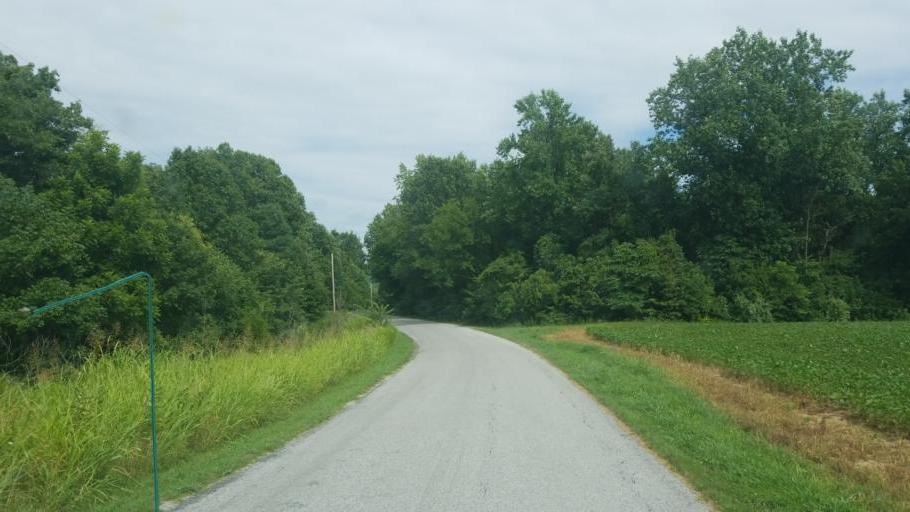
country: US
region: Illinois
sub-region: Union County
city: Cobden
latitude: 37.6125
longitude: -89.3465
